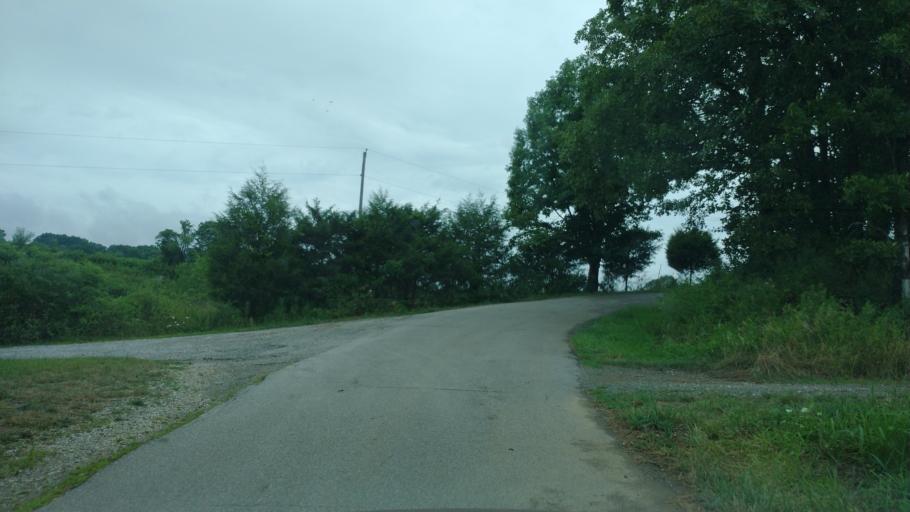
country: US
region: West Virginia
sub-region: Mason County
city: New Haven
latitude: 38.9242
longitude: -81.9547
